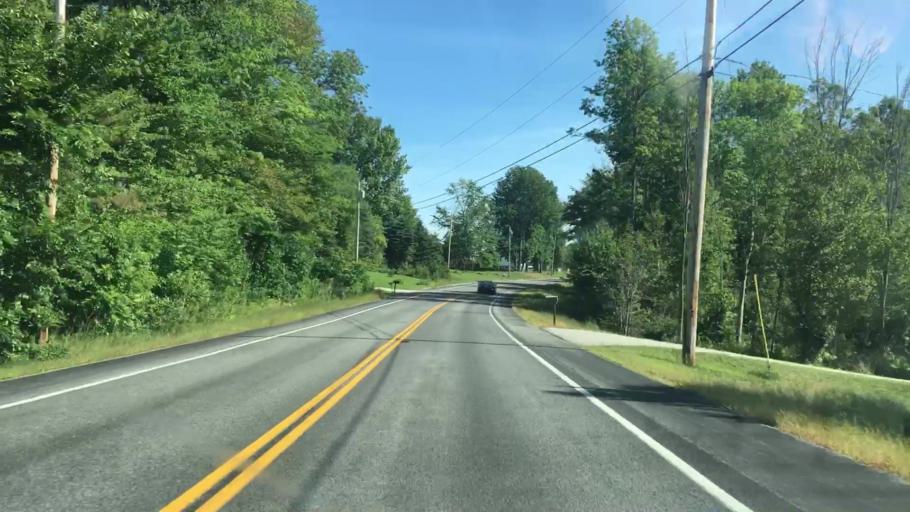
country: US
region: Maine
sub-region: Androscoggin County
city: Lisbon
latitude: 44.0332
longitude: -70.0702
